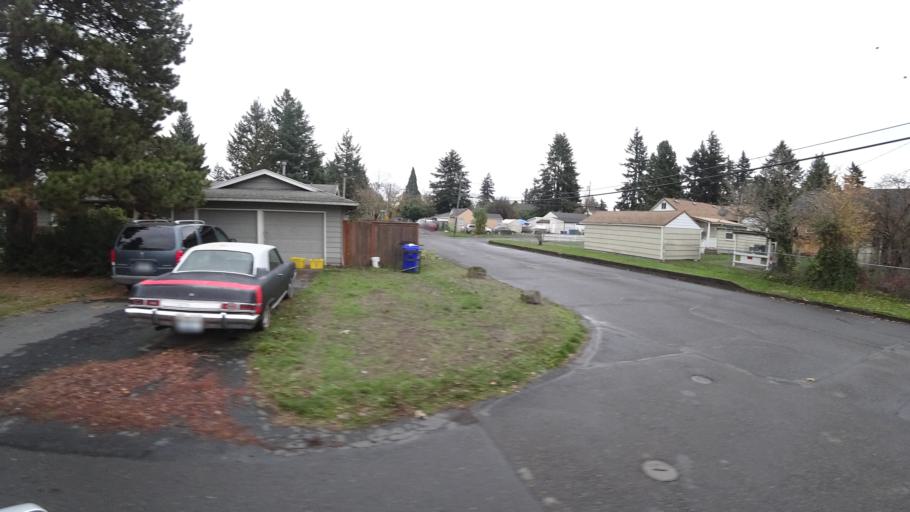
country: US
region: Oregon
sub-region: Multnomah County
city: Lents
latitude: 45.5300
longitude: -122.5415
